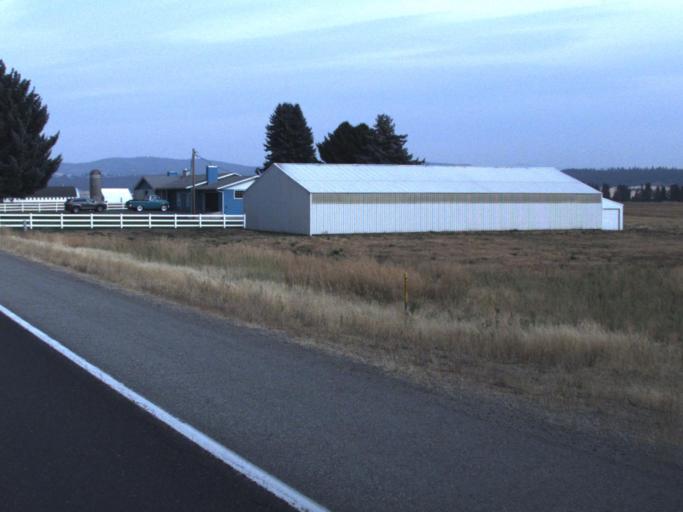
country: US
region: Washington
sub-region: Spokane County
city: Mead
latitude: 47.7873
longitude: -117.3302
